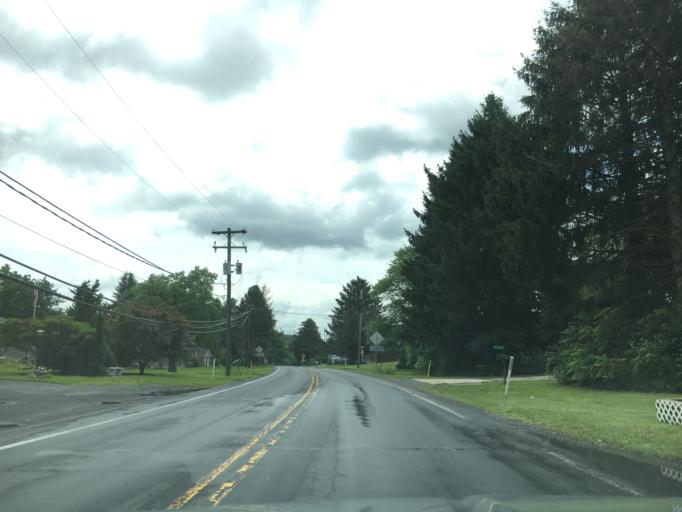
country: US
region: Pennsylvania
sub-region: Lehigh County
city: Laurys Station
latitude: 40.7238
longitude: -75.5309
